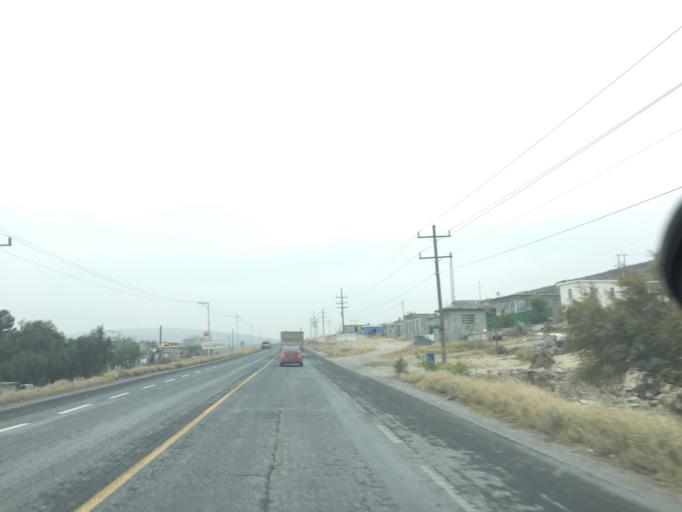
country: MX
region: Nuevo Leon
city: Mina
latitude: 26.0048
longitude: -100.5419
